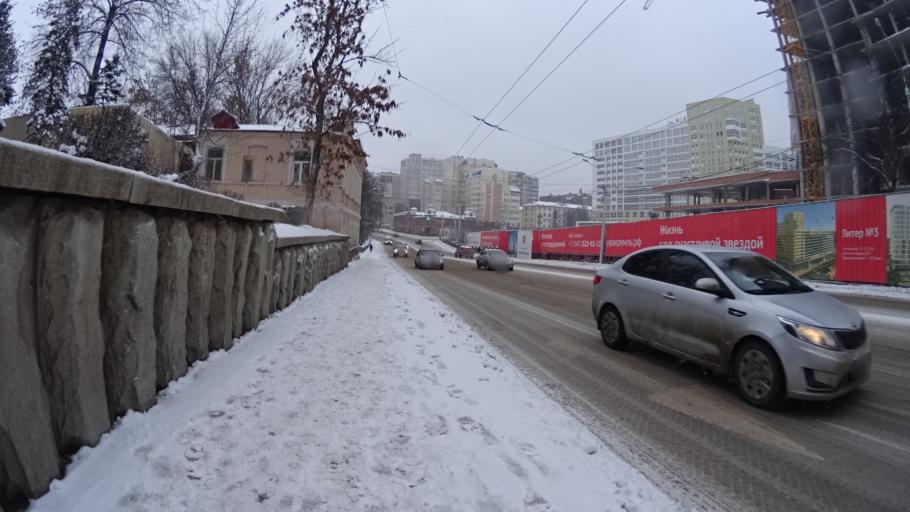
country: RU
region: Bashkortostan
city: Ufa
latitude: 54.7239
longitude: 55.9517
